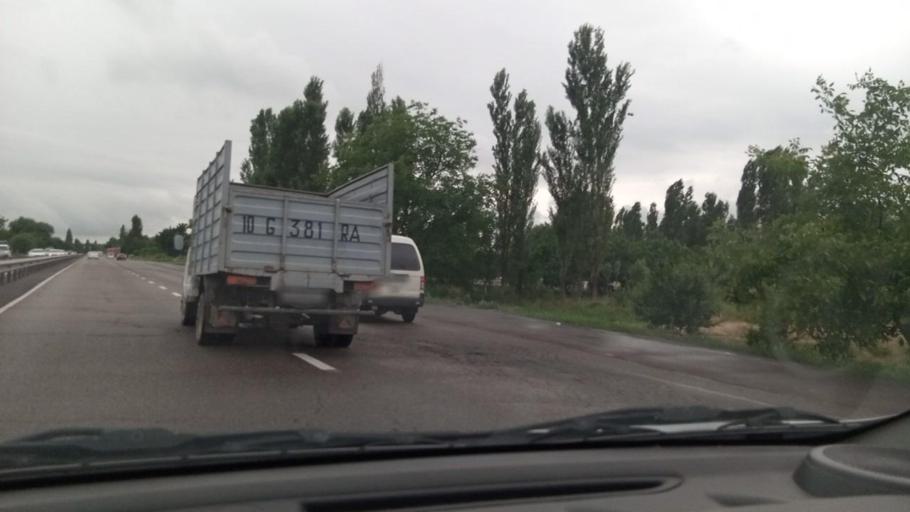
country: UZ
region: Toshkent
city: Ohangaron
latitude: 40.9086
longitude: 69.7781
